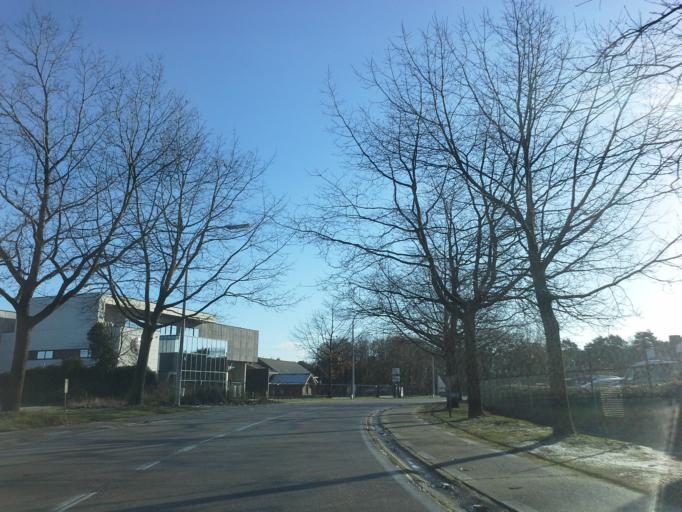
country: BE
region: Flanders
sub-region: Provincie Antwerpen
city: Herentals
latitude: 51.1598
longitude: 4.8139
